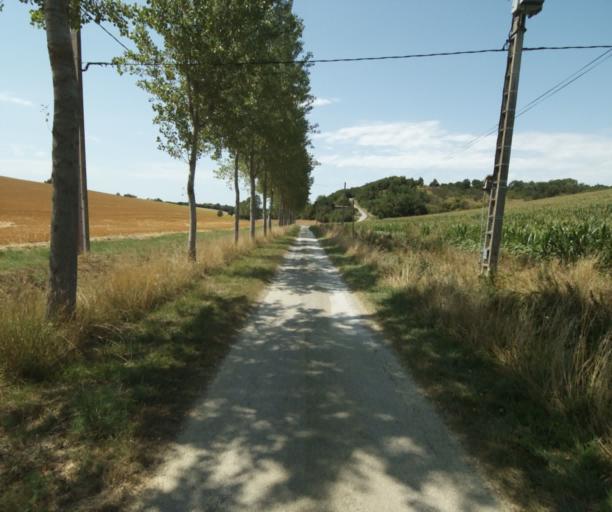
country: FR
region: Midi-Pyrenees
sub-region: Departement de la Haute-Garonne
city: Saint-Felix-Lauragais
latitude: 43.4634
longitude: 1.8609
